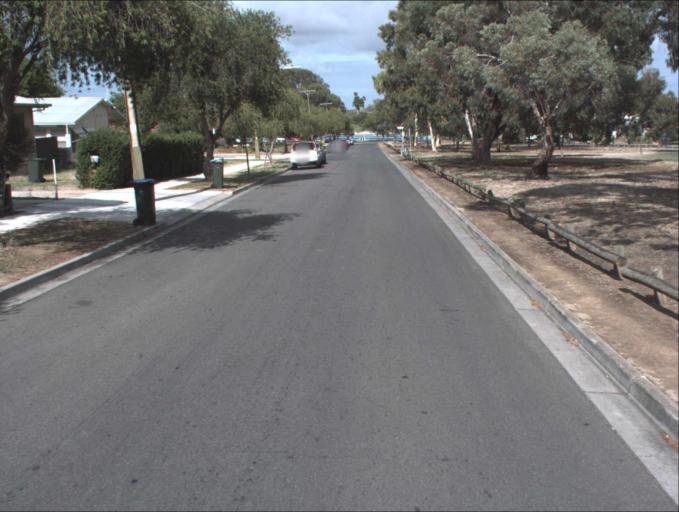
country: AU
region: South Australia
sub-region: Port Adelaide Enfield
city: Gilles Plains
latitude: -34.8525
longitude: 138.6626
